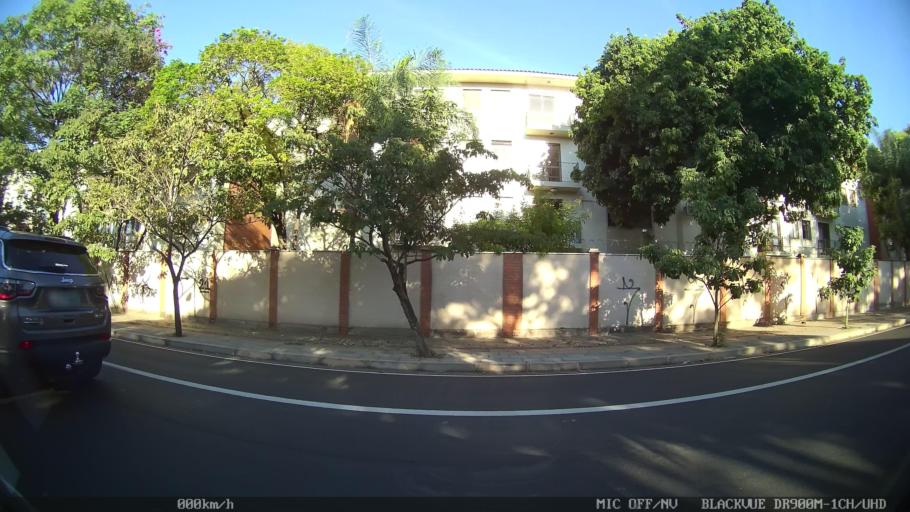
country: BR
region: Sao Paulo
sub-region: Sao Jose Do Rio Preto
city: Sao Jose do Rio Preto
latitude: -20.8233
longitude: -49.4011
